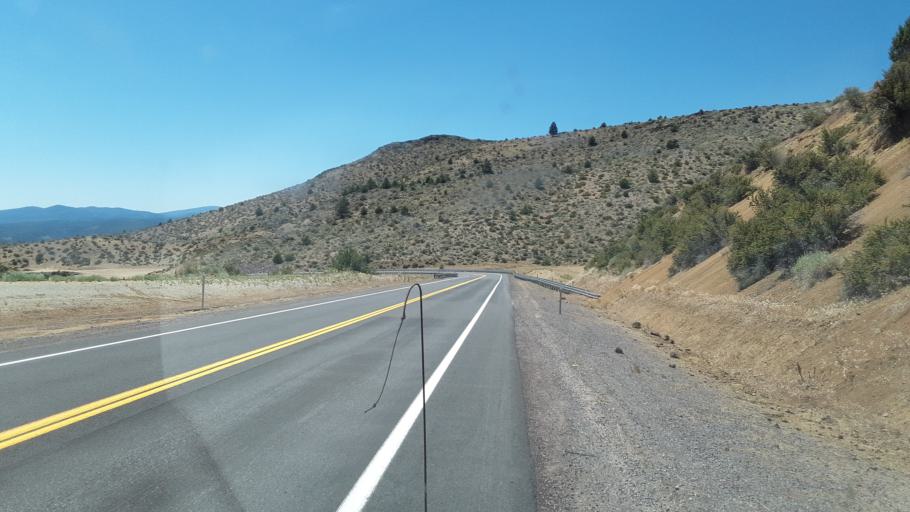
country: US
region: California
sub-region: Lassen County
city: Johnstonville
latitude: 40.4630
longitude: -120.5732
